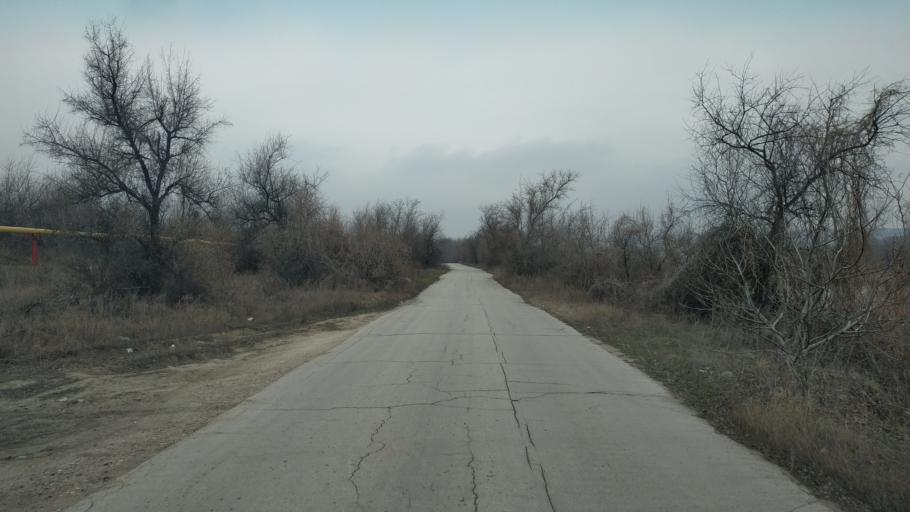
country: MD
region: Chisinau
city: Singera
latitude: 46.9186
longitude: 29.0082
